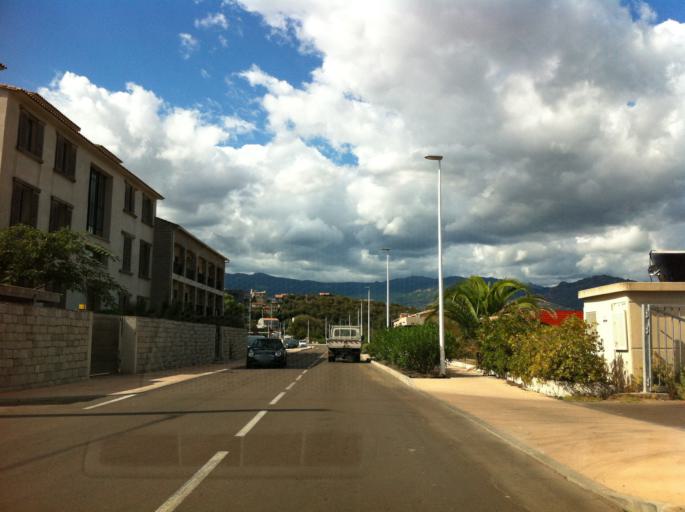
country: FR
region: Corsica
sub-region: Departement de la Corse-du-Sud
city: Porto-Vecchio
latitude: 41.5874
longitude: 9.2893
